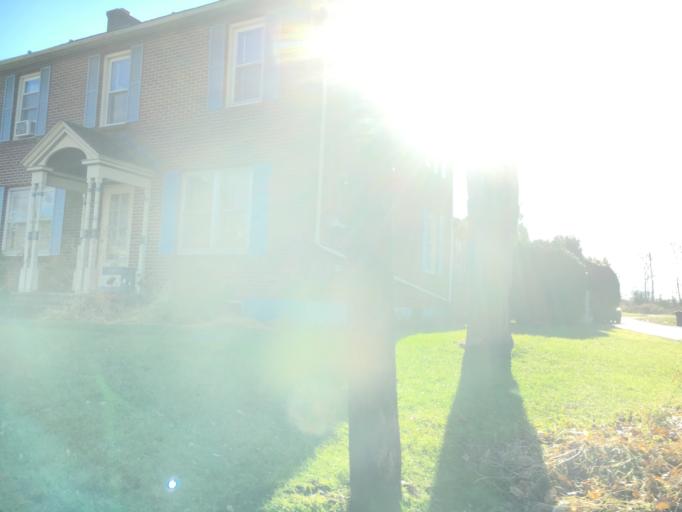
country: US
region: Pennsylvania
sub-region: Lehigh County
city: Stiles
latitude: 40.6485
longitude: -75.5146
